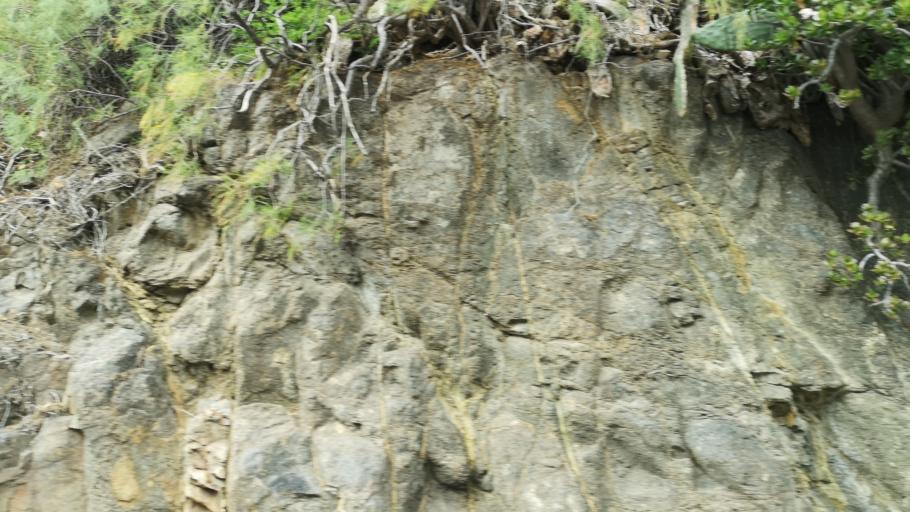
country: ES
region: Canary Islands
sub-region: Provincia de Santa Cruz de Tenerife
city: Vallehermosa
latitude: 28.1888
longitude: -17.2627
